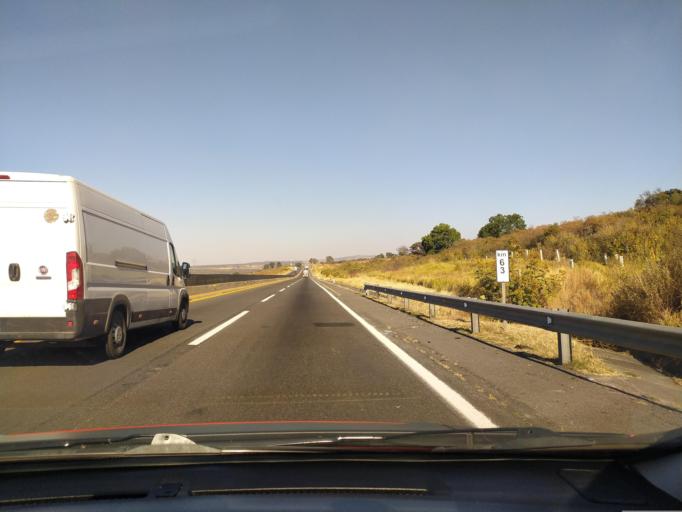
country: MX
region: Jalisco
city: Valle de Guadalupe
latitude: 20.9554
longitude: -102.6405
